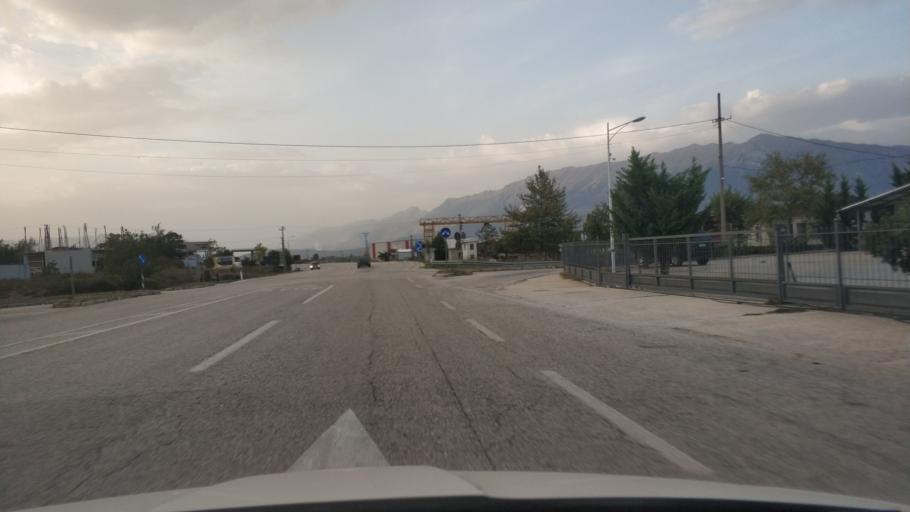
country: AL
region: Gjirokaster
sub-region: Rrethi i Gjirokastres
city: Dervician
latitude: 39.9970
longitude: 20.2161
